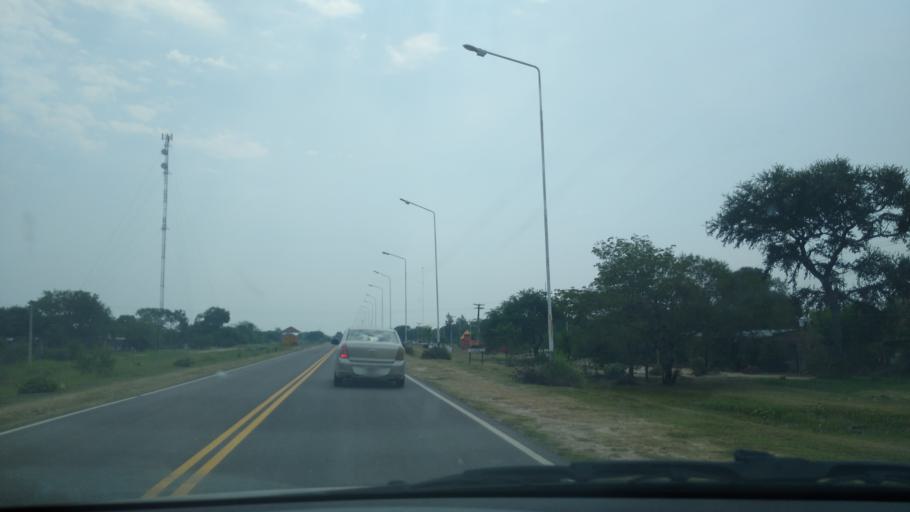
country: AR
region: Chaco
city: La Eduvigis
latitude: -26.8377
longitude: -59.0618
